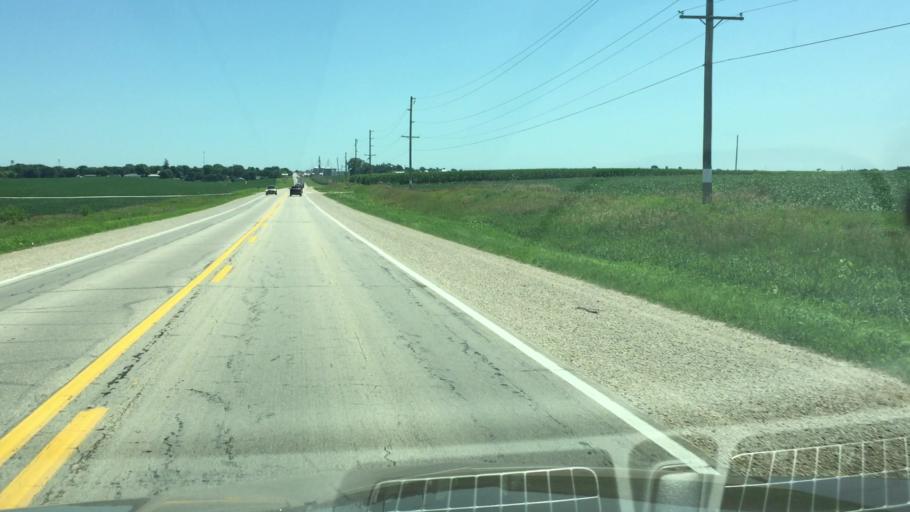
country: US
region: Iowa
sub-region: Cedar County
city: Mechanicsville
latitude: 41.8885
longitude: -91.1742
